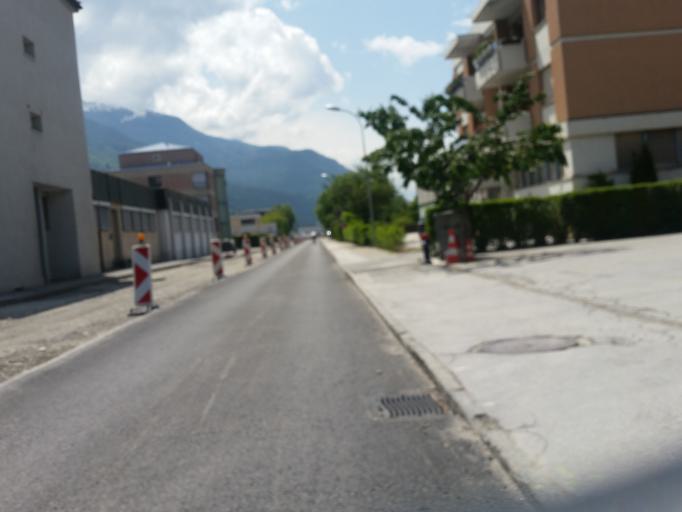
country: CH
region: Valais
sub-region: Sion District
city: Sitten
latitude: 46.2267
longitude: 7.3657
